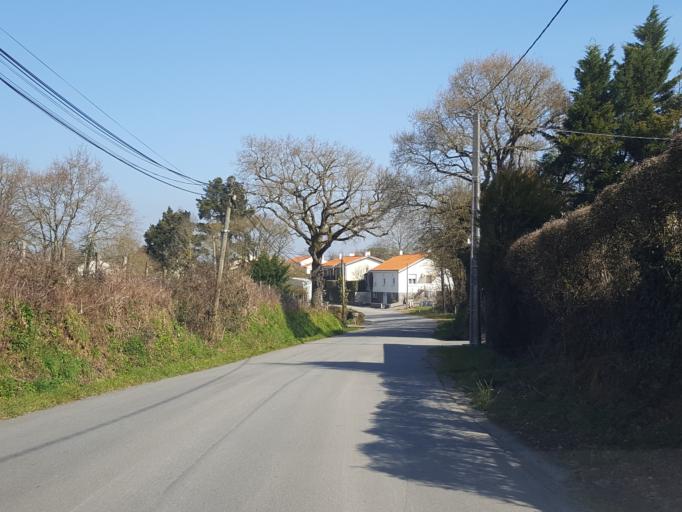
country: FR
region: Pays de la Loire
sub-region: Departement de la Vendee
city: La Chaize-le-Vicomte
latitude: 46.6671
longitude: -1.2942
